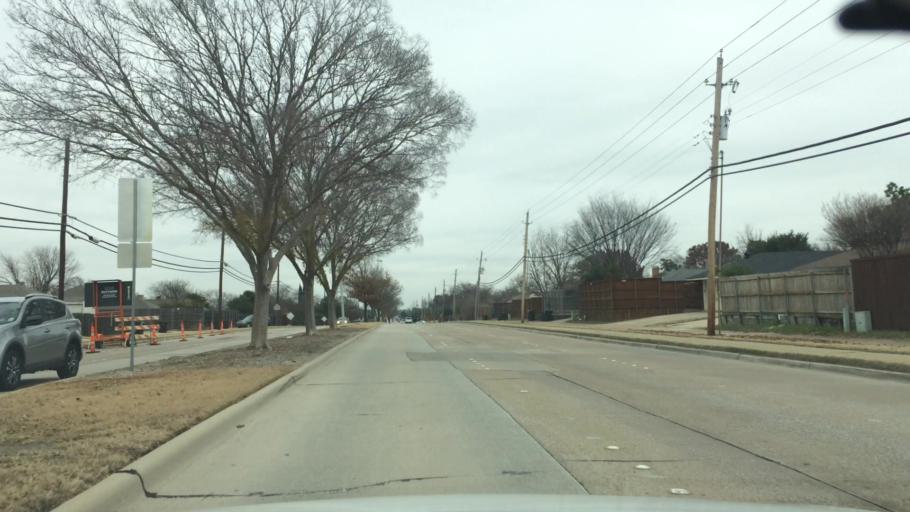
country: US
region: Texas
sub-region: Collin County
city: Plano
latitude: 33.0410
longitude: -96.7433
